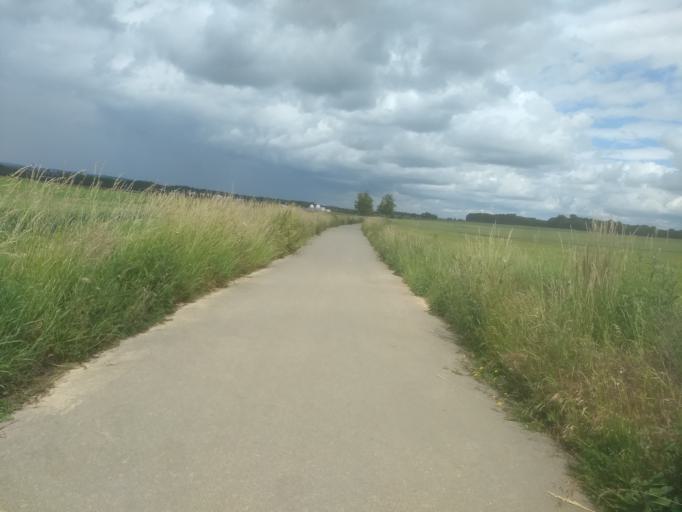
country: FR
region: Nord-Pas-de-Calais
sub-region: Departement du Pas-de-Calais
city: Riviere
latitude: 50.2578
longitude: 2.7050
